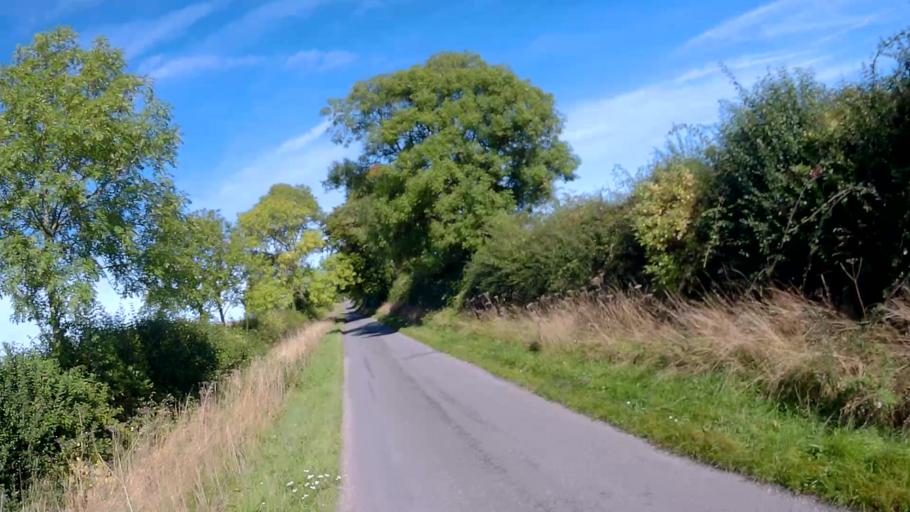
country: GB
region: England
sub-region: Hampshire
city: Andover
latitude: 51.1632
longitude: -1.4001
